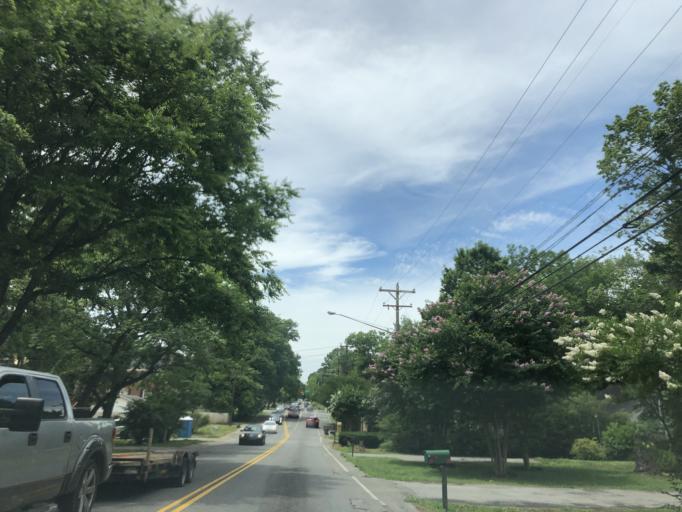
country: US
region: Tennessee
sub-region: Davidson County
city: Oak Hill
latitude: 36.1108
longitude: -86.7857
